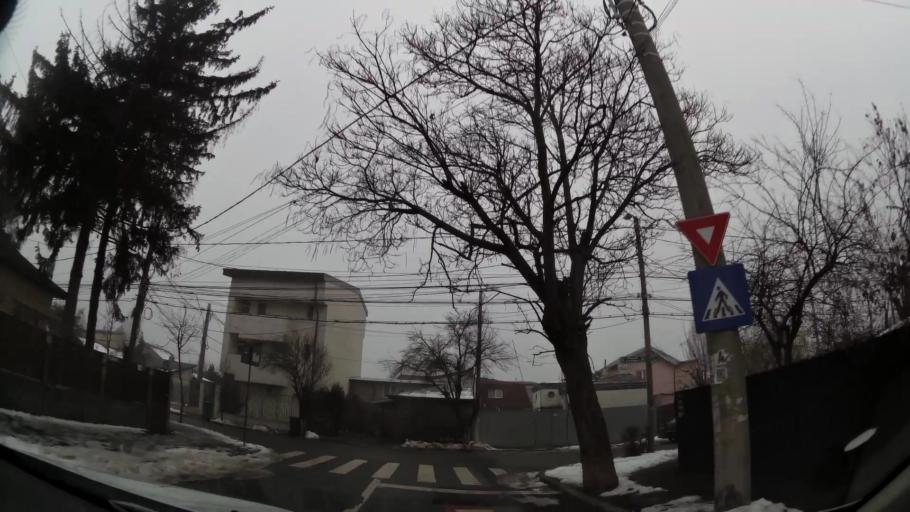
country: RO
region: Ilfov
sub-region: Comuna Chiajna
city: Rosu
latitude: 44.4788
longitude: 26.0331
